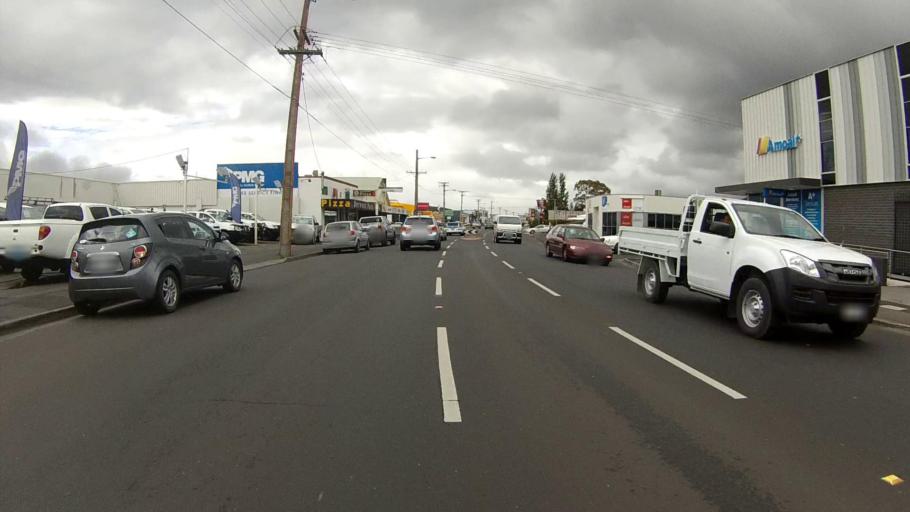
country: AU
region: Tasmania
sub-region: Glenorchy
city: Goodwood
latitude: -42.8363
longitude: 147.2872
